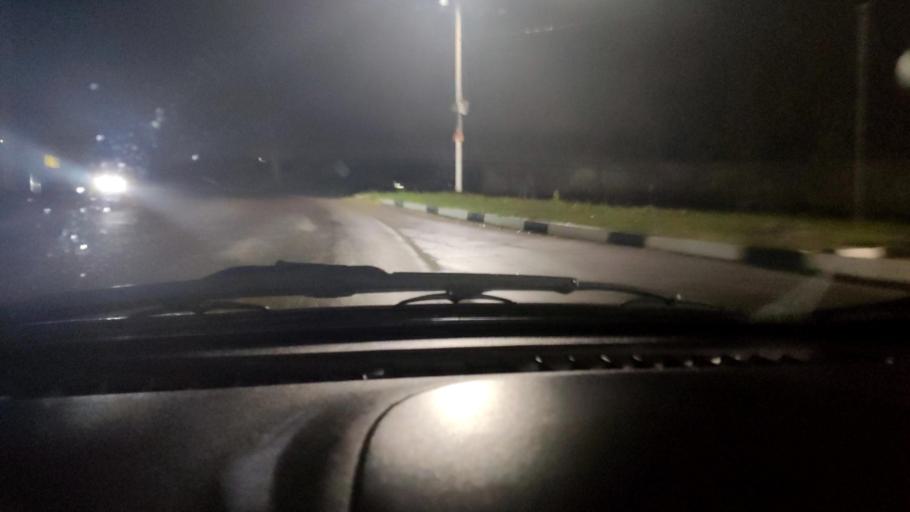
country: RU
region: Voronezj
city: Latnaya
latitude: 51.6608
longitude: 38.9062
